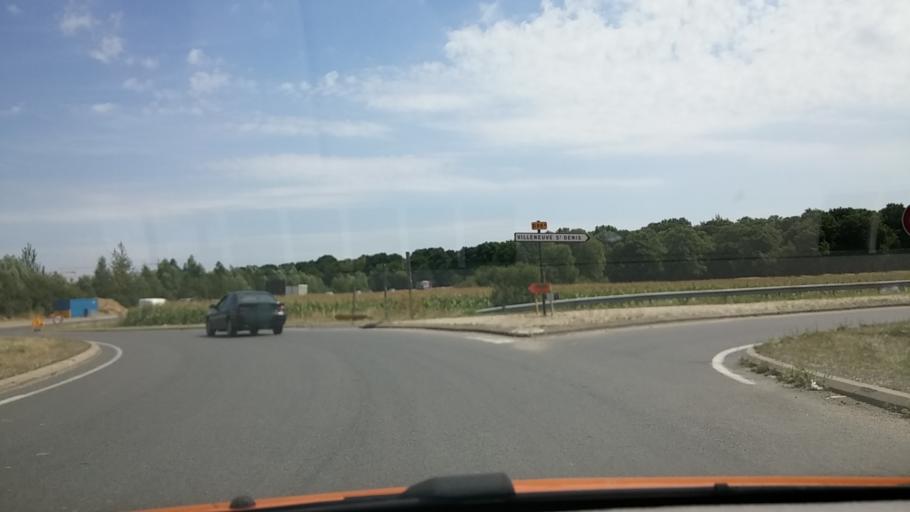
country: FR
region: Ile-de-France
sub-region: Departement de Seine-et-Marne
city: Serris
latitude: 48.8312
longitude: 2.7983
